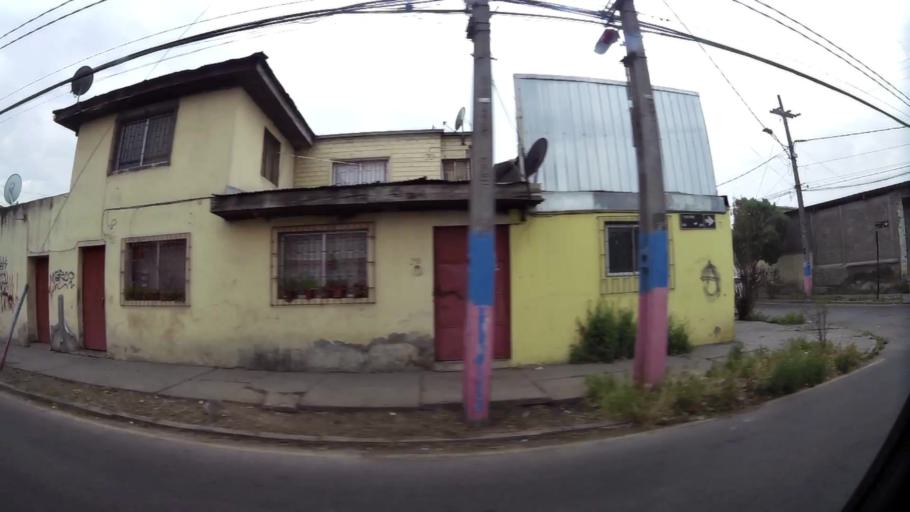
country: CL
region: Santiago Metropolitan
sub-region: Provincia de Santiago
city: Santiago
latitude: -33.4773
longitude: -70.6648
